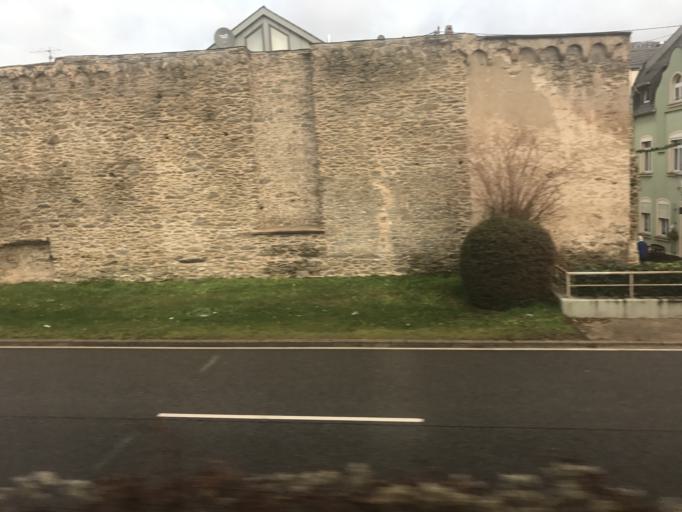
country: DE
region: Rheinland-Pfalz
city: Boppard
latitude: 50.2303
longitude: 7.5945
